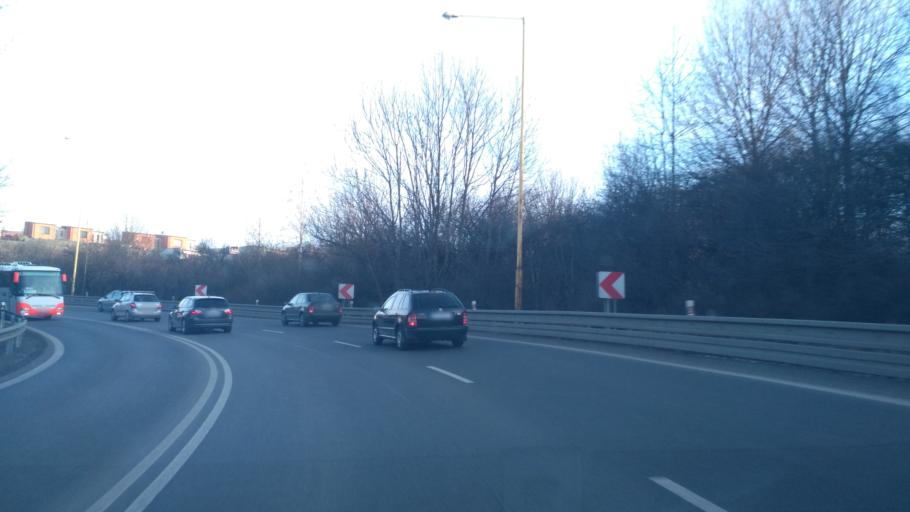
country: SK
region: Kosicky
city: Kosice
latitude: 48.7217
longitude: 21.2899
